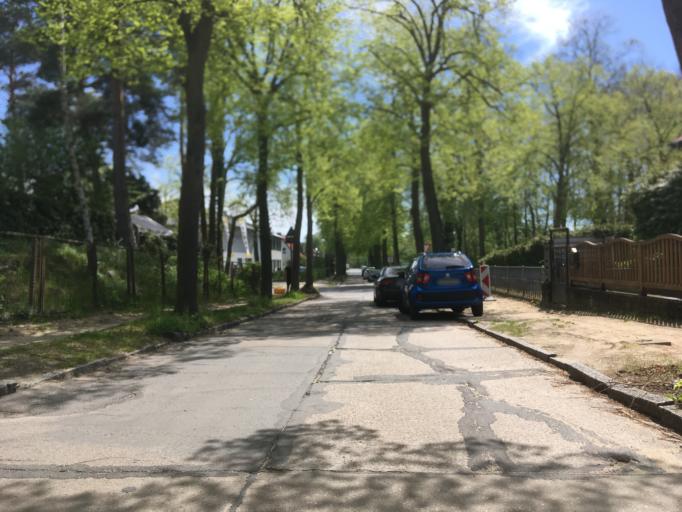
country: DE
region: Brandenburg
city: Zeuthen
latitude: 52.3443
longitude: 13.6085
